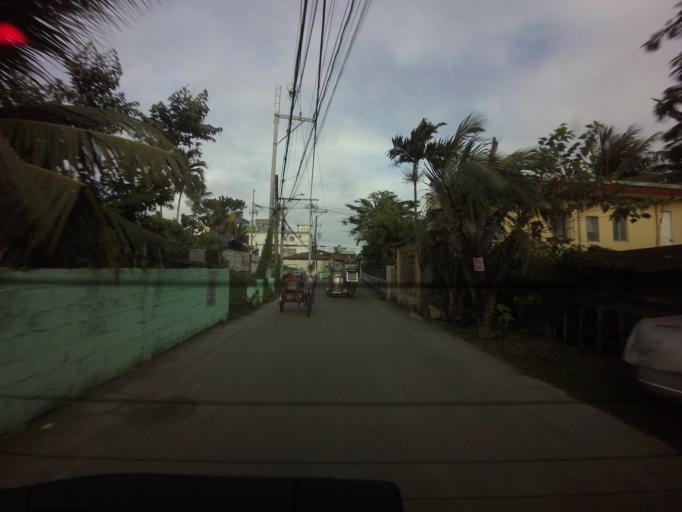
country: PH
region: Central Luzon
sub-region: Province of Bulacan
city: Obando
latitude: 14.7109
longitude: 120.9436
